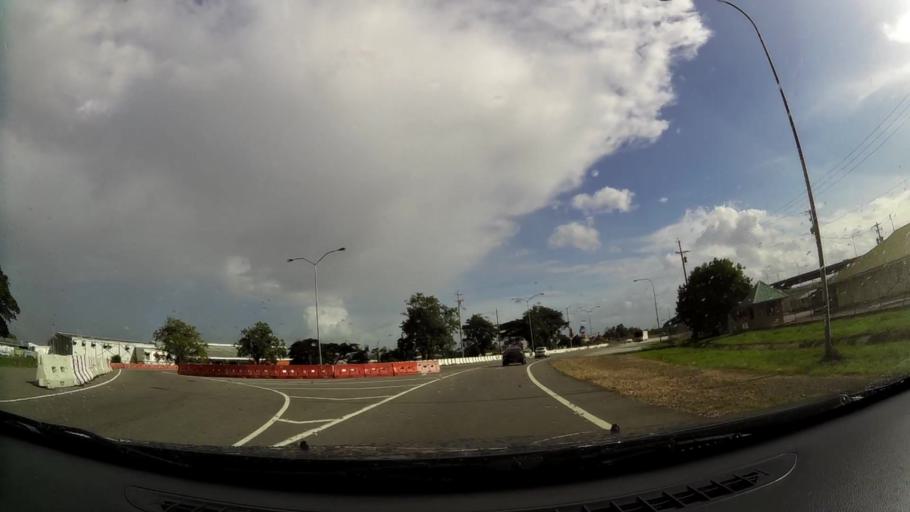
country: TT
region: Tunapuna/Piarco
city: Tunapuna
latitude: 10.6345
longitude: -61.4296
